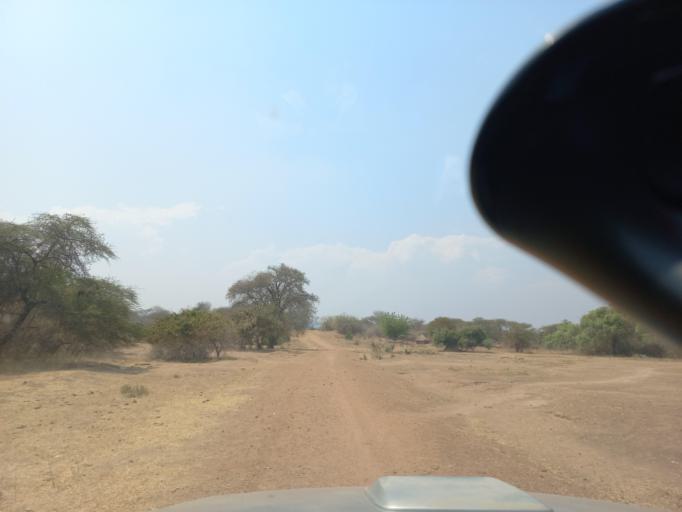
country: ZW
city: Chirundu
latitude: -15.9140
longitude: 28.6865
